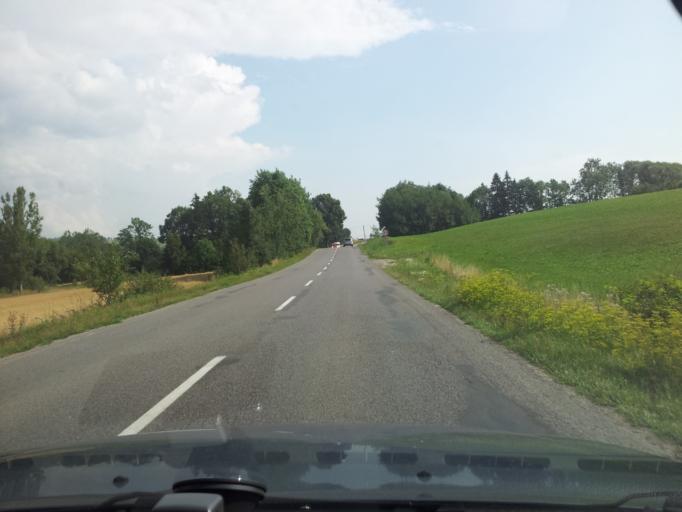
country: SK
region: Zilinsky
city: Namestovo
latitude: 49.3799
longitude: 19.4330
